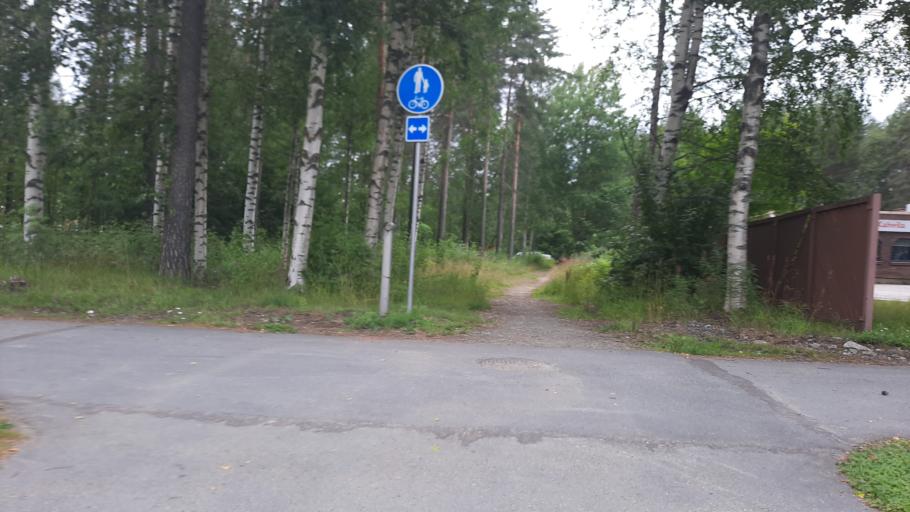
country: FI
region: North Karelia
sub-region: Joensuu
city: Joensuu
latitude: 62.6139
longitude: 29.8138
